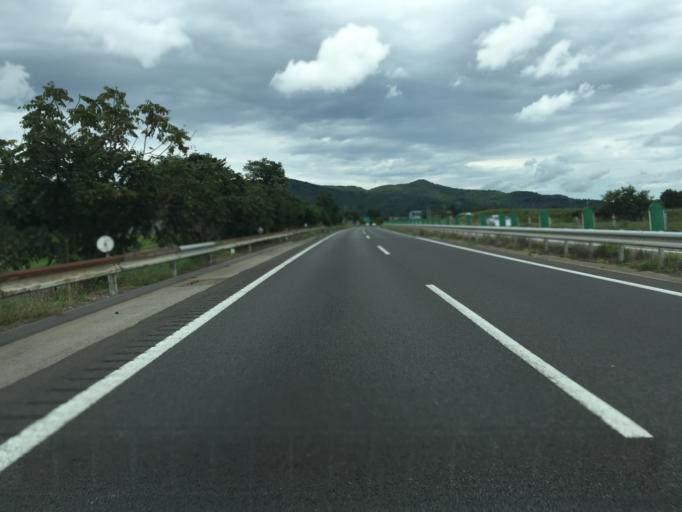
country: JP
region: Miyagi
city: Shiroishi
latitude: 38.0300
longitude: 140.6256
